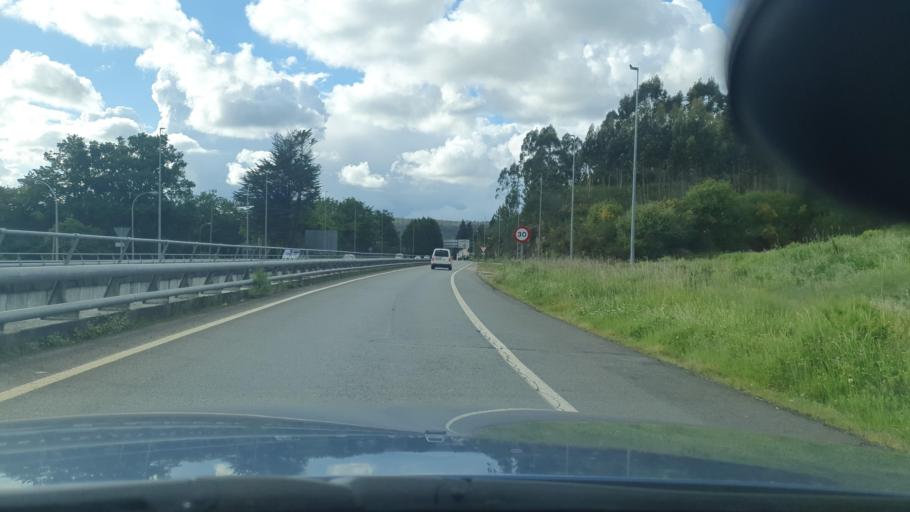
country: ES
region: Galicia
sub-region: Provincia da Coruna
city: Santiago de Compostela
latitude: 42.8696
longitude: -8.5764
